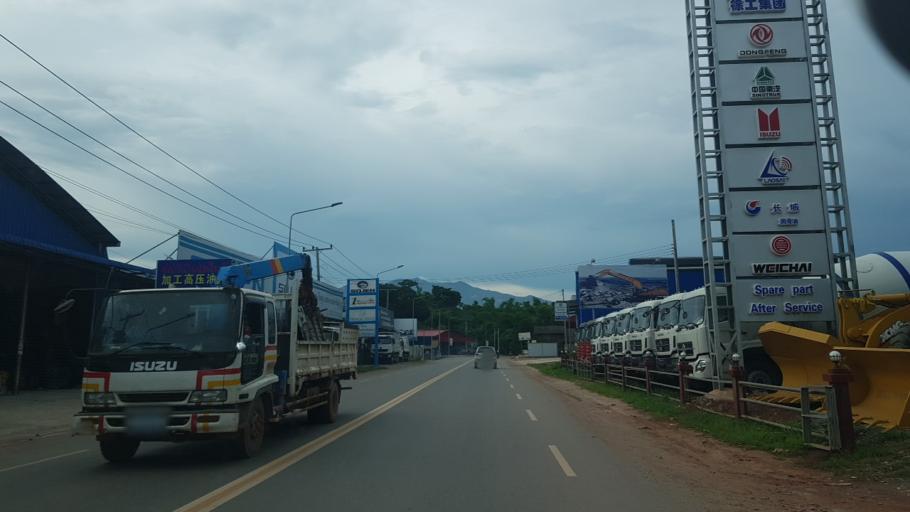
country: LA
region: Oudomxai
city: Muang Xay
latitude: 20.6696
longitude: 101.9828
